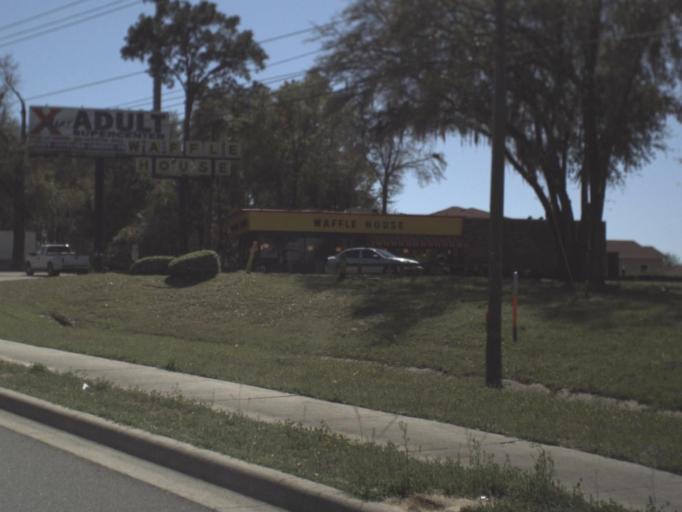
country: US
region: Florida
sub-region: Leon County
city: Tallahassee
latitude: 30.4737
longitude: -84.3630
